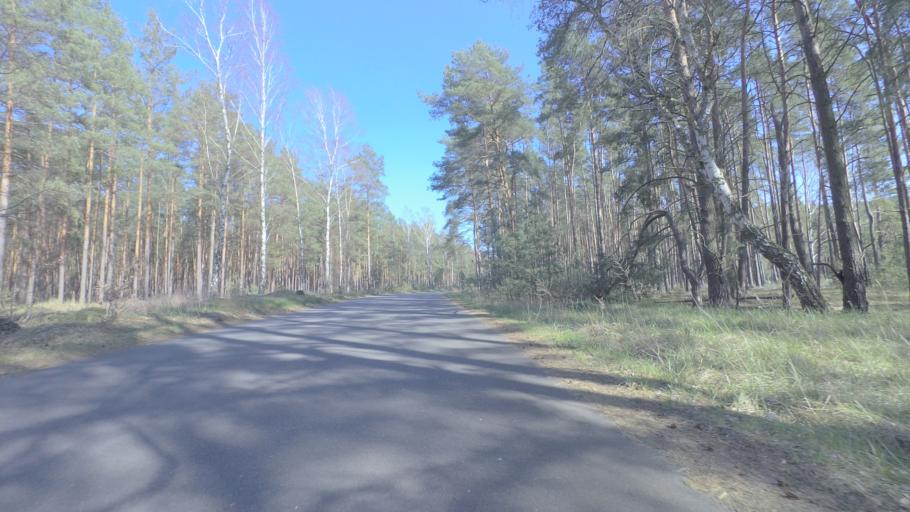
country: DE
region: Brandenburg
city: Munchehofe
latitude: 52.1635
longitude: 13.8030
